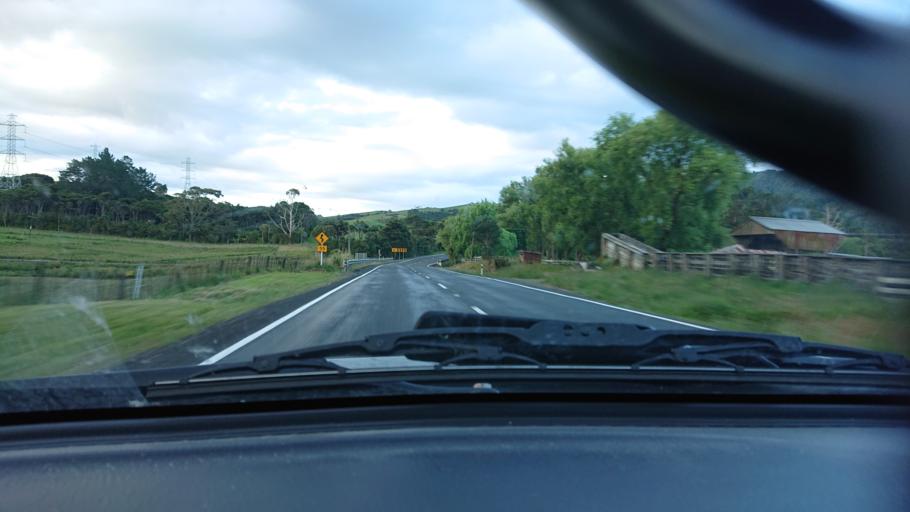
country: NZ
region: Auckland
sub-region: Auckland
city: Parakai
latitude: -36.4630
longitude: 174.4455
